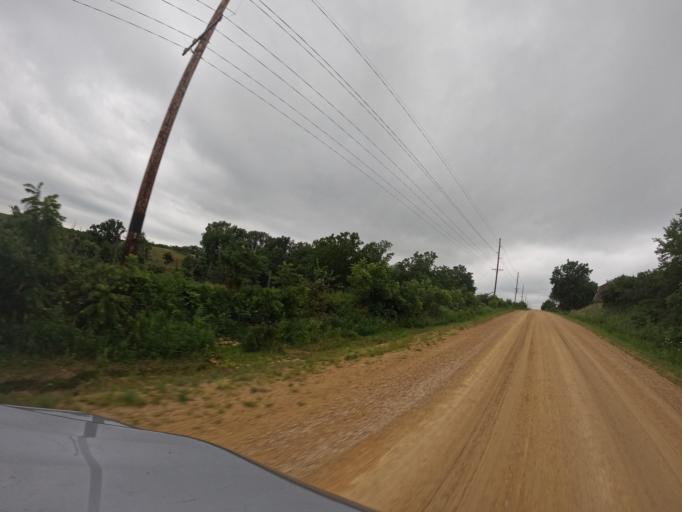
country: US
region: Iowa
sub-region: Jackson County
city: Maquoketa
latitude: 41.9380
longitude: -90.6300
